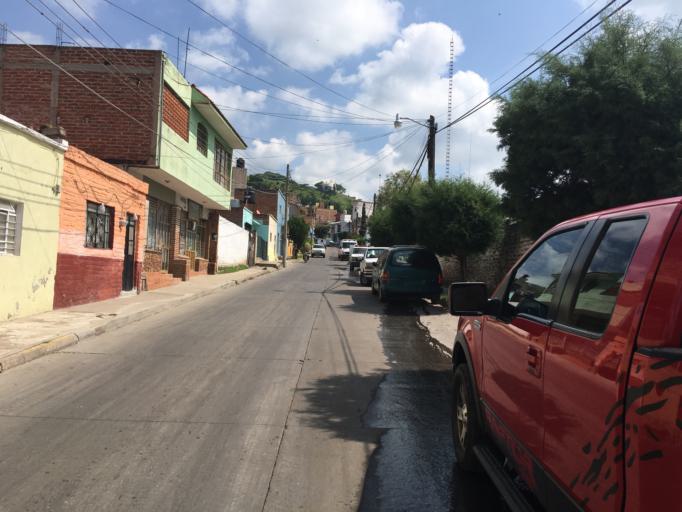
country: MX
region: Jalisco
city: Atotonilco el Alto
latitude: 20.5487
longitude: -102.5139
